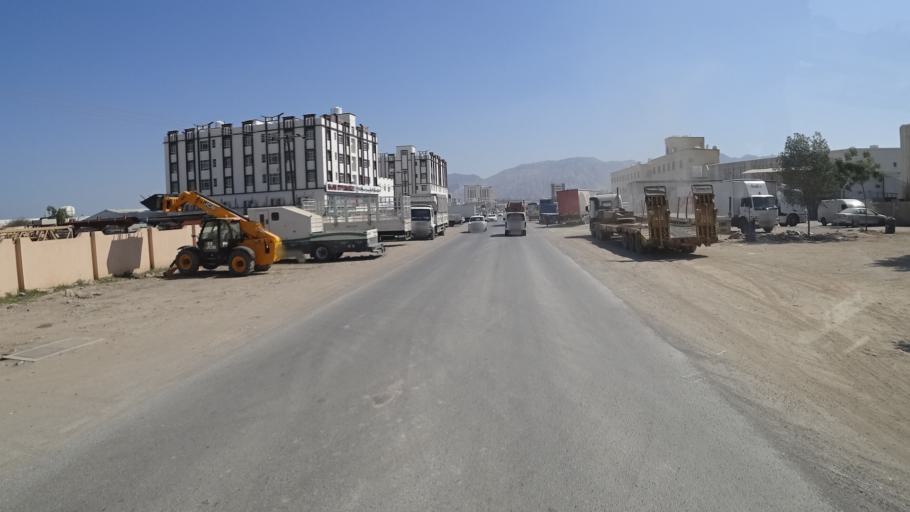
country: OM
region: Muhafazat Masqat
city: Bawshar
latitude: 23.5757
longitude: 58.3688
